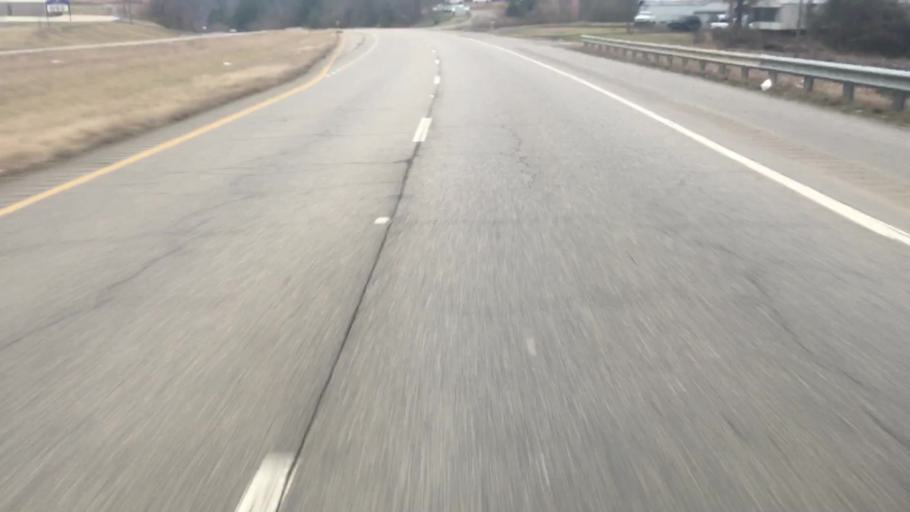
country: US
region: Alabama
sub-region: Walker County
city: Dora
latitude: 33.7959
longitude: -87.1095
